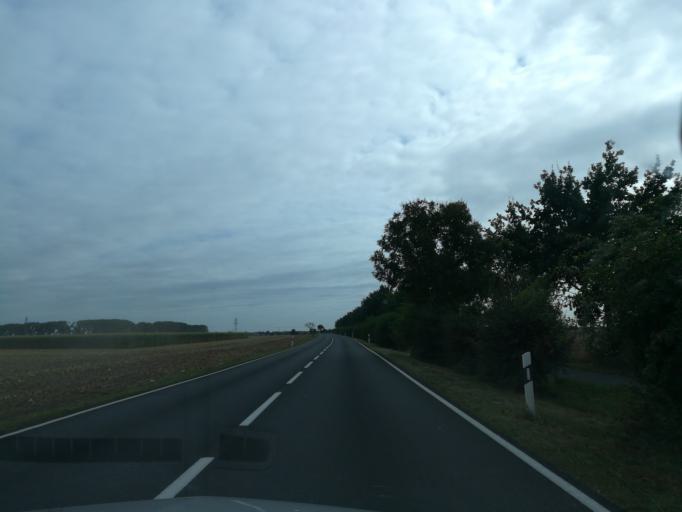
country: DE
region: Saxony-Anhalt
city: Meitzendorf
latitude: 52.2022
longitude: 11.5558
